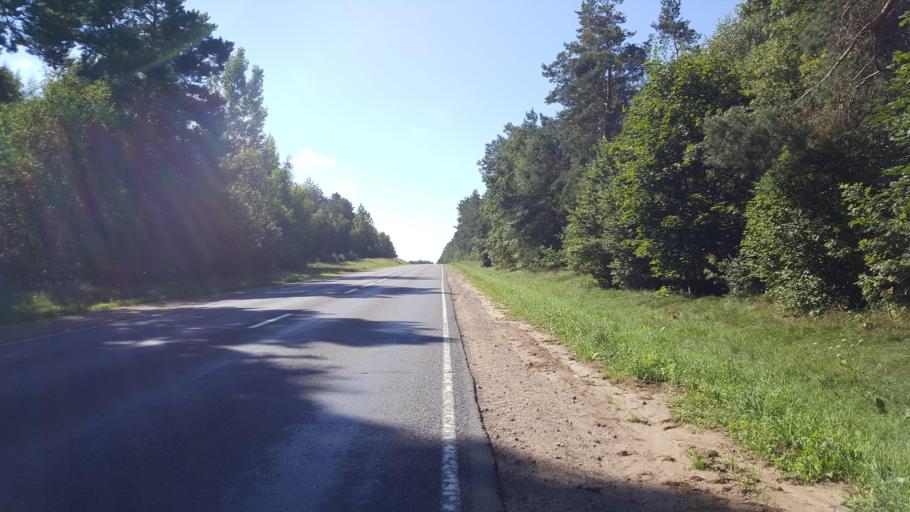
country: BY
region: Brest
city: Kamyanyets
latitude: 52.3507
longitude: 23.7773
